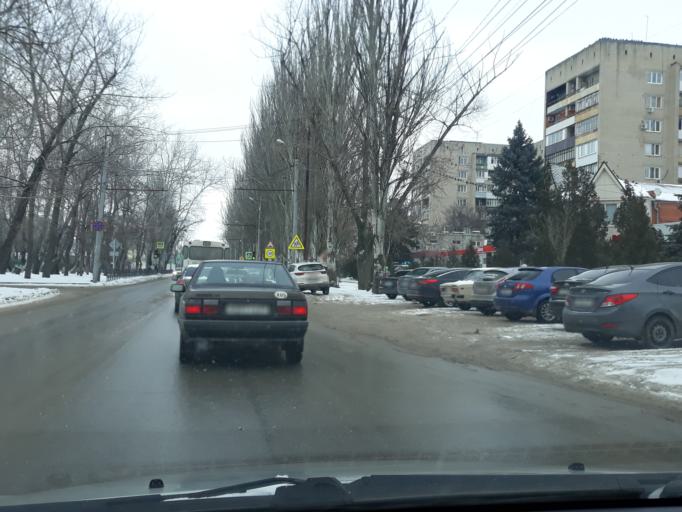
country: RU
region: Rostov
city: Taganrog
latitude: 47.2466
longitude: 38.9177
